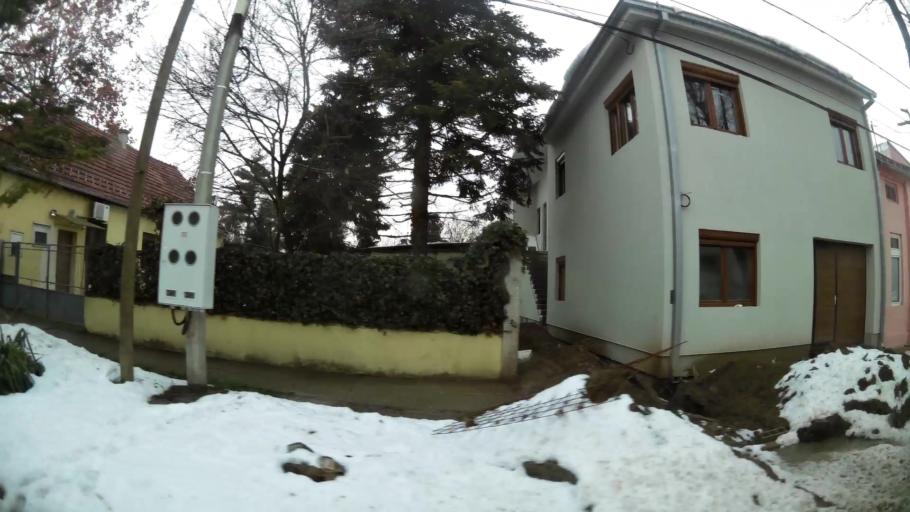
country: RS
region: Central Serbia
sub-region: Belgrade
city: Zemun
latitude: 44.8537
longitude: 20.3792
